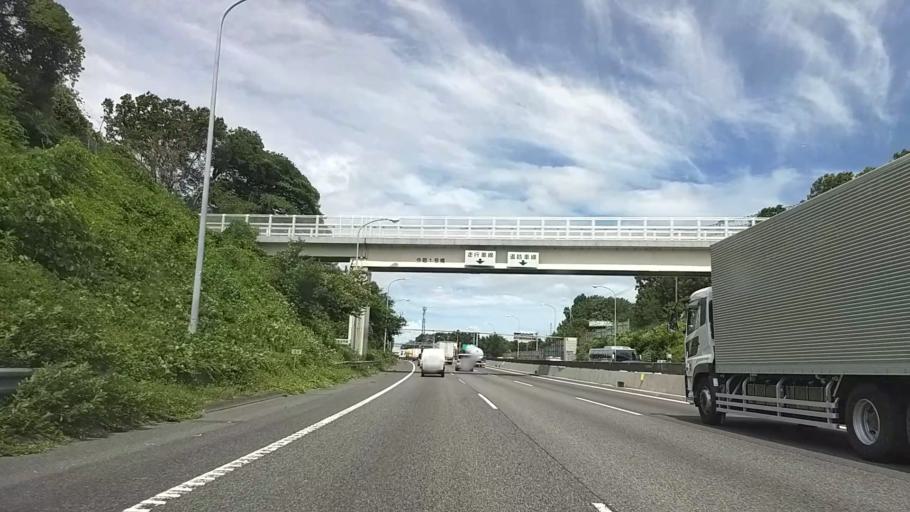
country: JP
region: Kanagawa
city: Minami-rinkan
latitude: 35.4762
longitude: 139.5269
